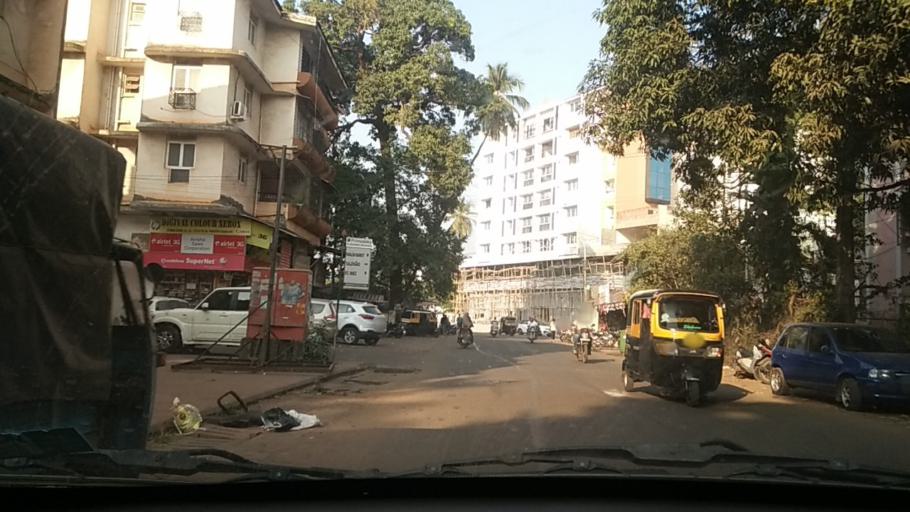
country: IN
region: Goa
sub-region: North Goa
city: Panaji
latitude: 15.4895
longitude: 73.8196
